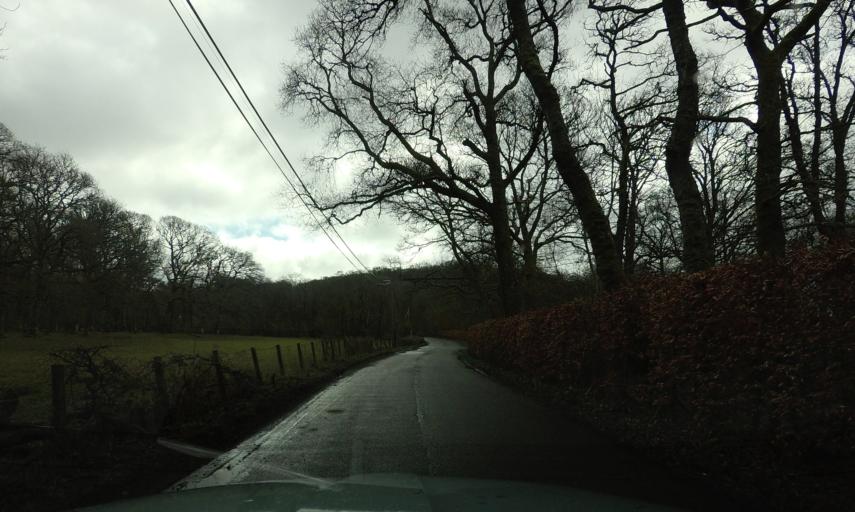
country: GB
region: Scotland
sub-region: West Dunbartonshire
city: Balloch
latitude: 56.0969
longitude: -4.5557
